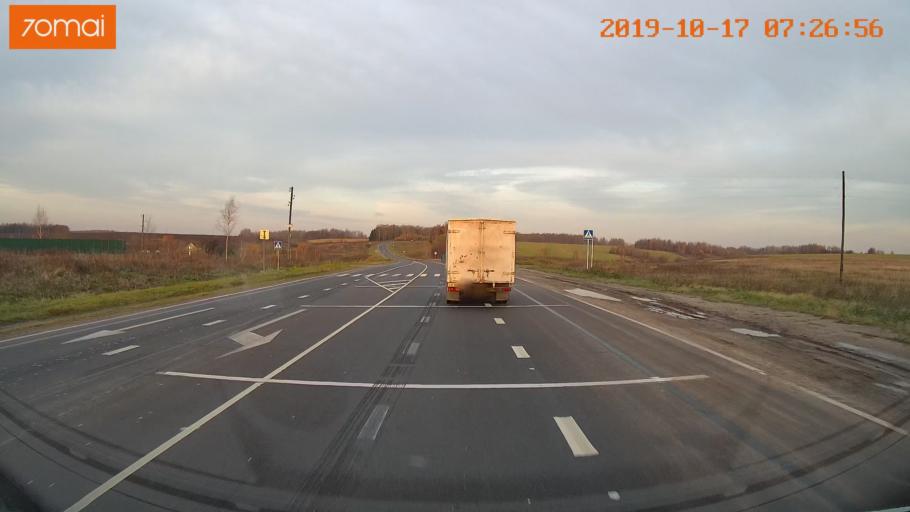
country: RU
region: Ivanovo
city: Gavrilov Posad
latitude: 56.3601
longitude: 40.0866
